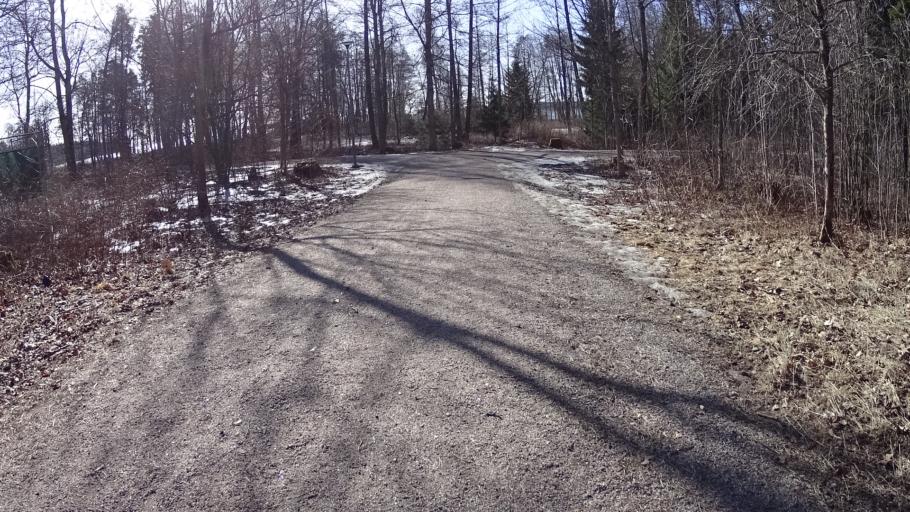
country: FI
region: Uusimaa
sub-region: Helsinki
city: Koukkuniemi
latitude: 60.1577
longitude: 24.7857
